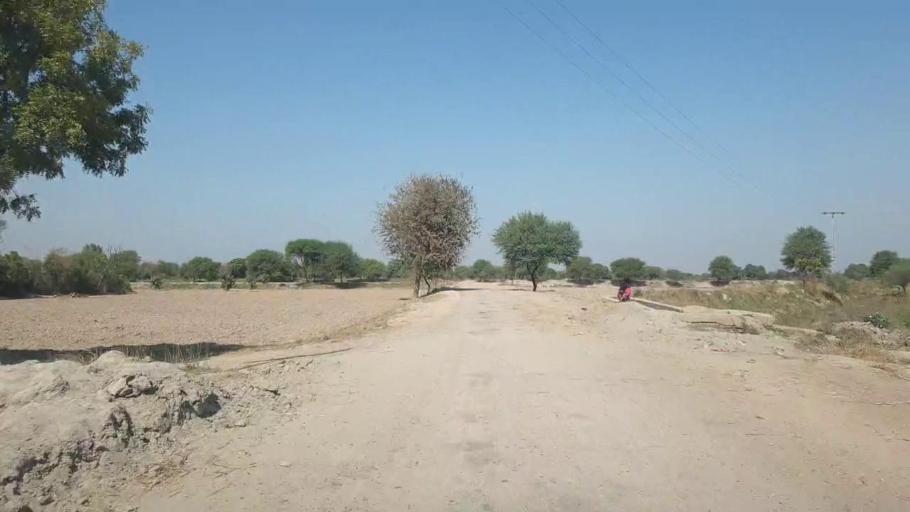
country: PK
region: Sindh
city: Chambar
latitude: 25.2971
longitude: 68.6918
